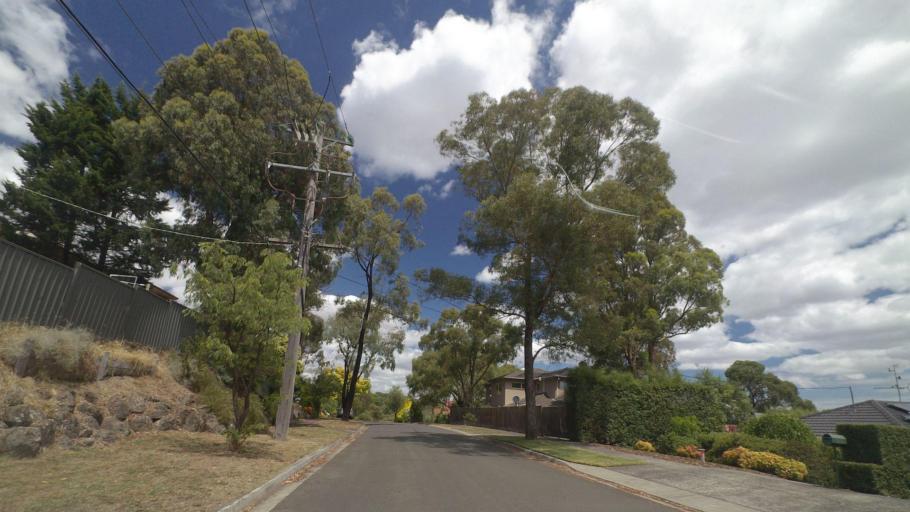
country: AU
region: Victoria
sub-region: Maroondah
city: Warranwood
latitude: -37.7777
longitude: 145.2426
